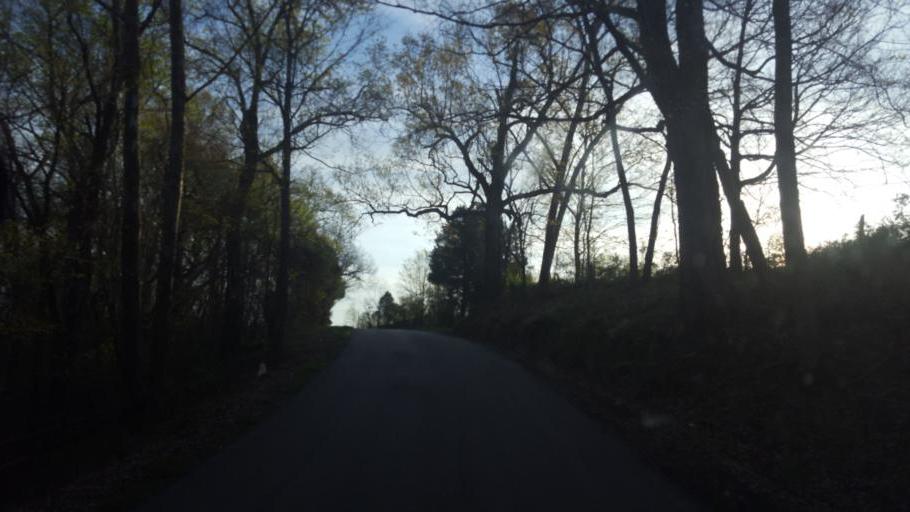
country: US
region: Kentucky
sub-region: Barren County
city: Cave City
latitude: 37.2083
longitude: -86.0150
